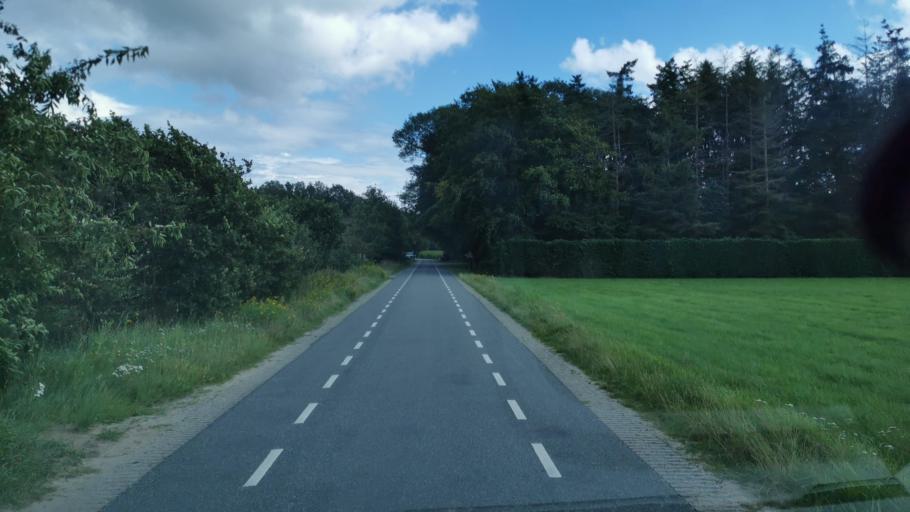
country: NL
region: Overijssel
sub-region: Gemeente Haaksbergen
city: Haaksbergen
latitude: 52.1506
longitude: 6.8189
